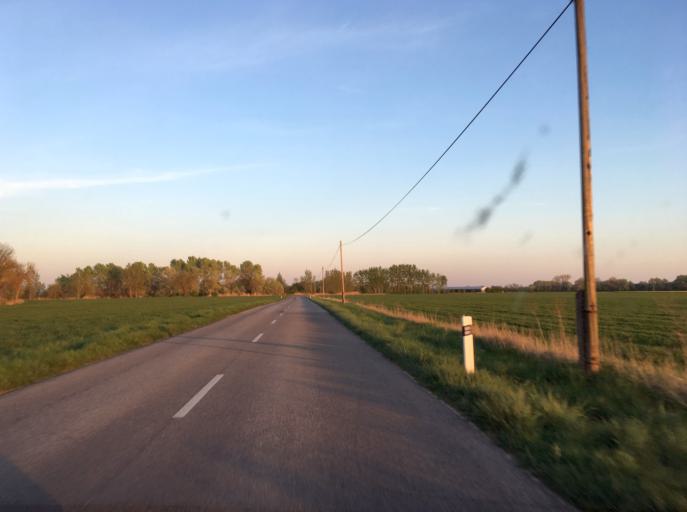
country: SK
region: Nitriansky
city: Kolarovo
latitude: 47.8785
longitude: 17.9122
